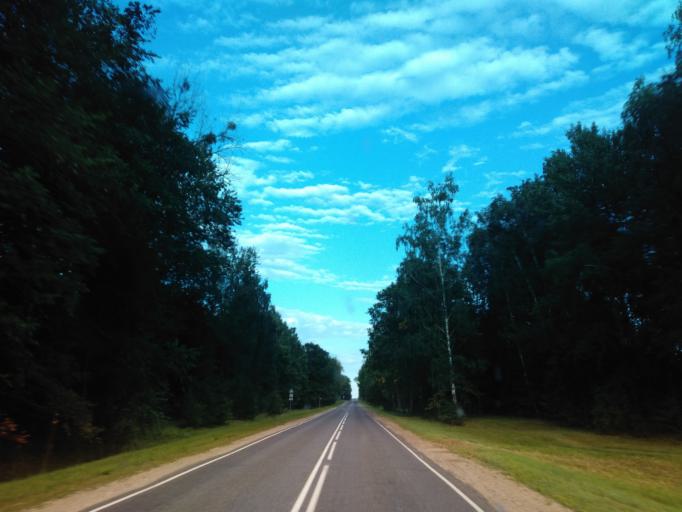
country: BY
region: Minsk
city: Uzda
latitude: 53.4401
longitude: 27.2922
